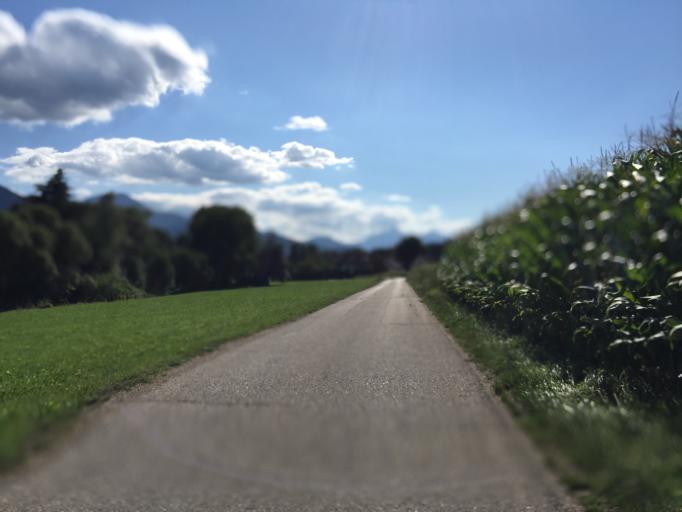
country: AT
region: Carinthia
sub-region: Politischer Bezirk Volkermarkt
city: Feistritz ob Bleiburg
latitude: 46.5696
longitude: 14.7573
